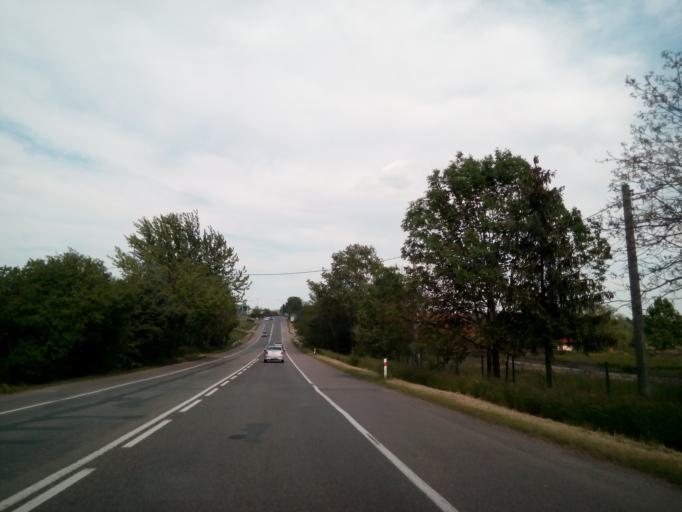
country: CZ
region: South Moravian
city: Tvarozna
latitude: 49.1838
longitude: 16.7538
